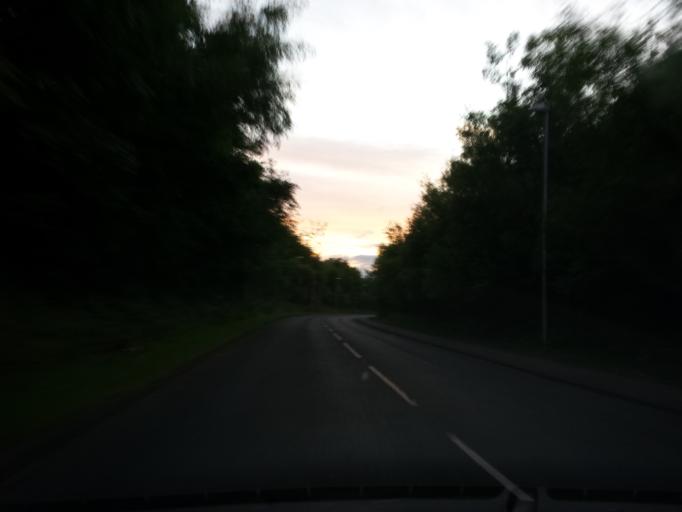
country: GB
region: Scotland
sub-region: The Scottish Borders
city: Eyemouth
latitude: 55.8676
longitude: -2.0956
